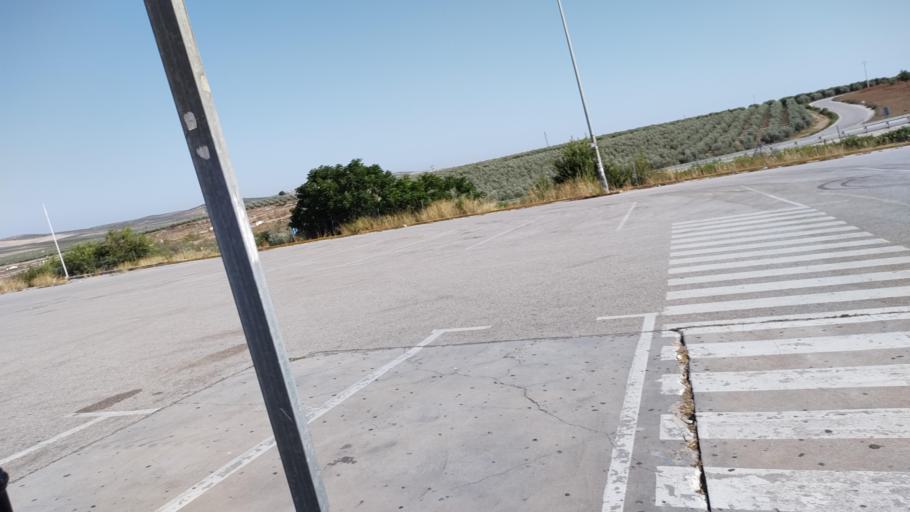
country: ES
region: Andalusia
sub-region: Provincia de Sevilla
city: Aguadulce
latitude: 37.2570
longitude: -4.9860
